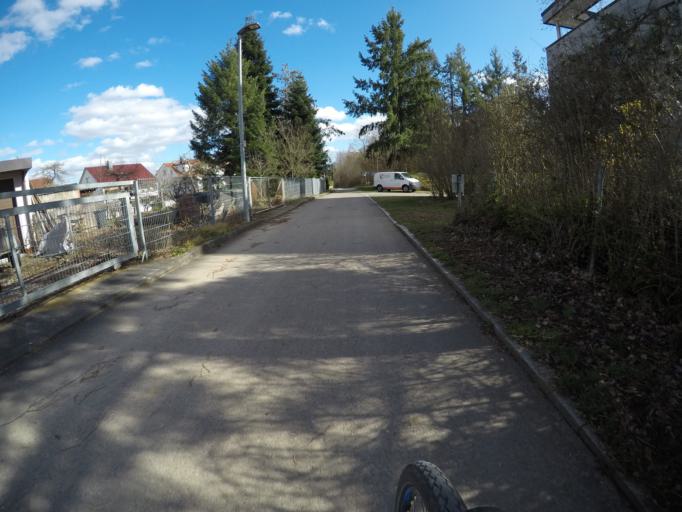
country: DE
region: Baden-Wuerttemberg
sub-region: Regierungsbezirk Stuttgart
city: Leinfelden-Echterdingen
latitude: 48.6598
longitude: 9.1815
